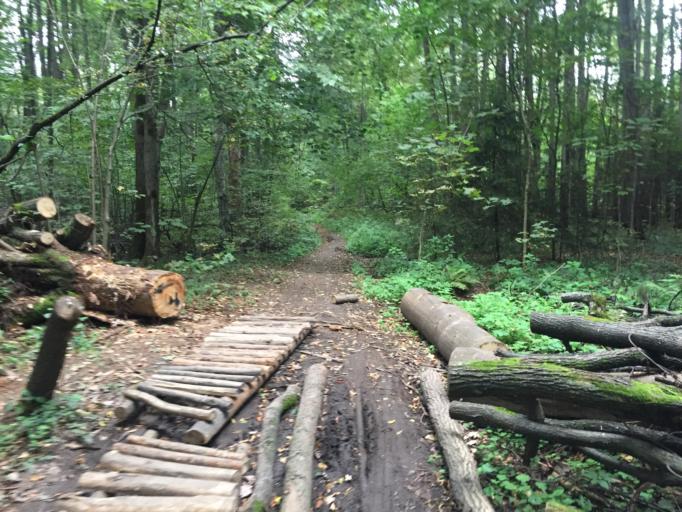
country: RU
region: Moscow
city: Babushkin
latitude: 55.8590
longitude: 37.7599
